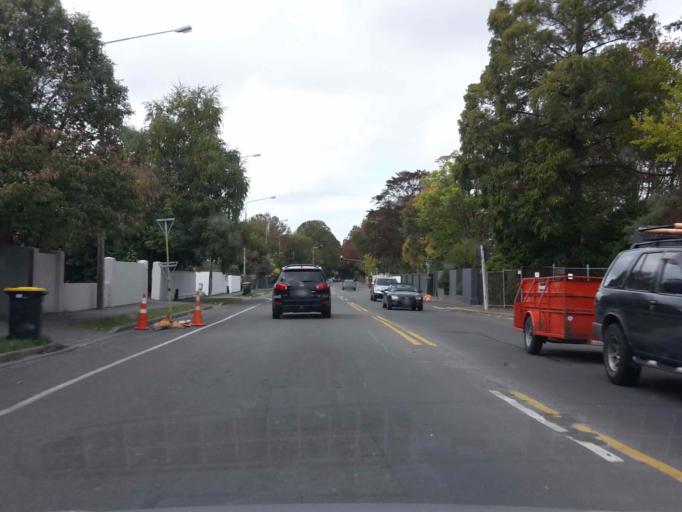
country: NZ
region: Canterbury
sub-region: Christchurch City
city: Christchurch
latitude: -43.5137
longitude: 172.6069
